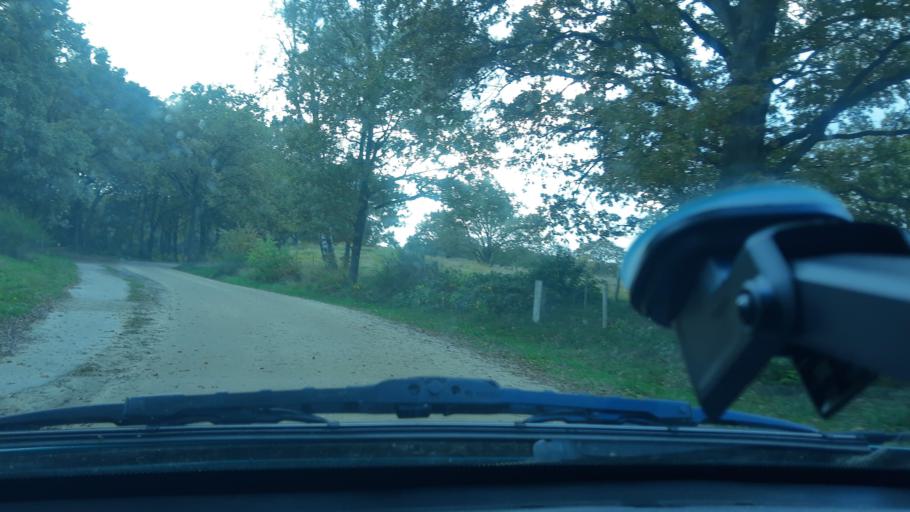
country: NL
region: Limburg
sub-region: Gemeente Gennep
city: Gennep
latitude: 51.6499
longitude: 6.0105
